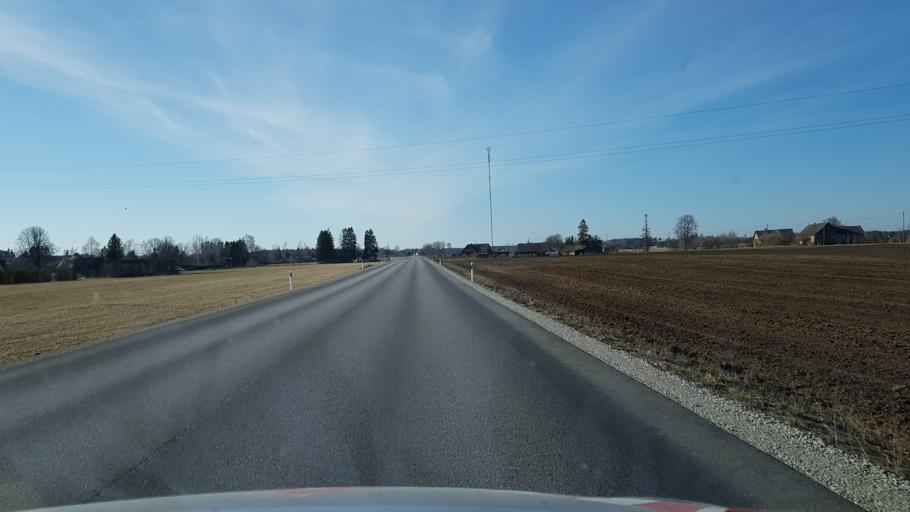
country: EE
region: Laeaene-Virumaa
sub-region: Vinni vald
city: Vinni
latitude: 59.2451
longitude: 26.4802
